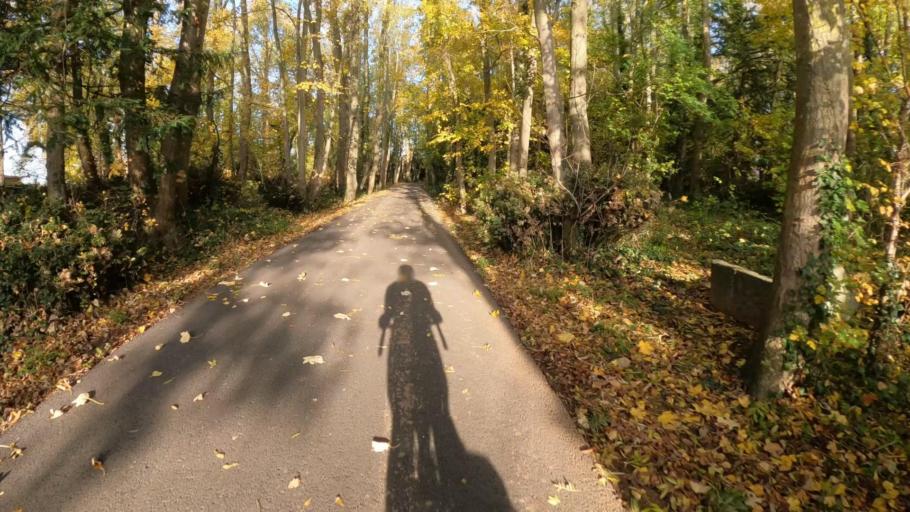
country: FR
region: Lower Normandy
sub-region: Departement du Calvados
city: Epron
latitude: 49.2141
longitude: -0.3411
